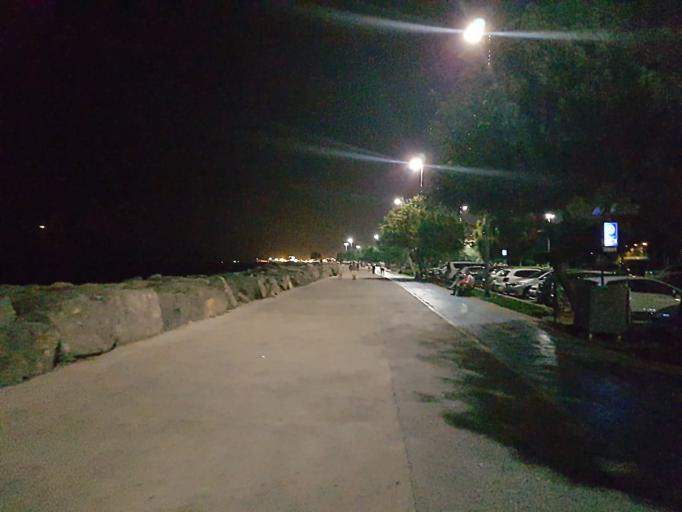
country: TR
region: Istanbul
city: Bahcelievler
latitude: 40.9551
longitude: 28.8212
